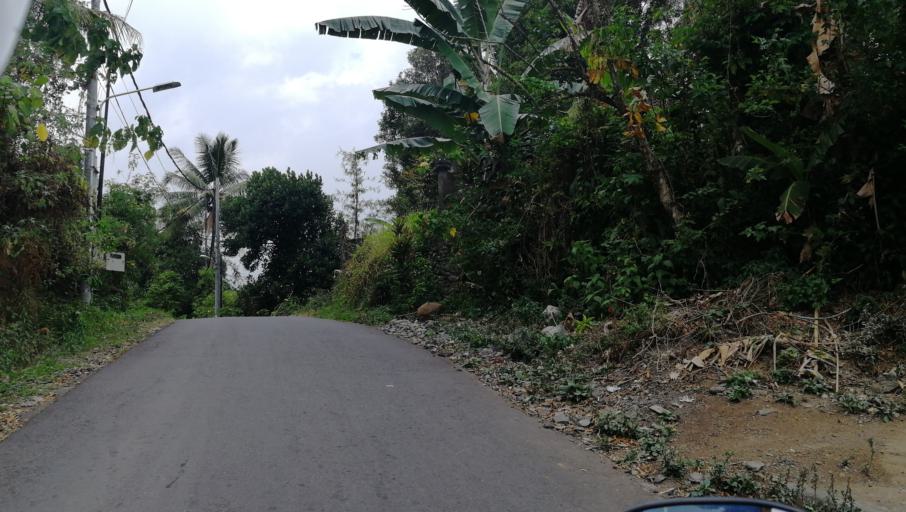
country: ID
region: Bali
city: Banjar Pedawa
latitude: -8.2637
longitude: 115.0409
